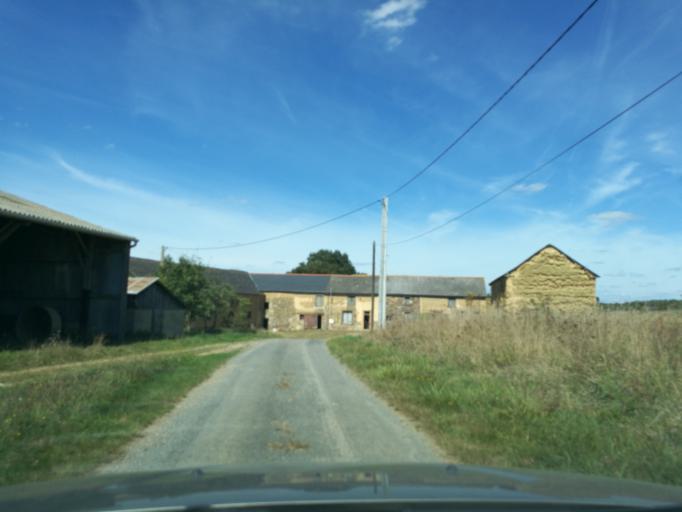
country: FR
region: Brittany
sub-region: Departement d'Ille-et-Vilaine
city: Bedee
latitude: 48.1608
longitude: -1.9553
